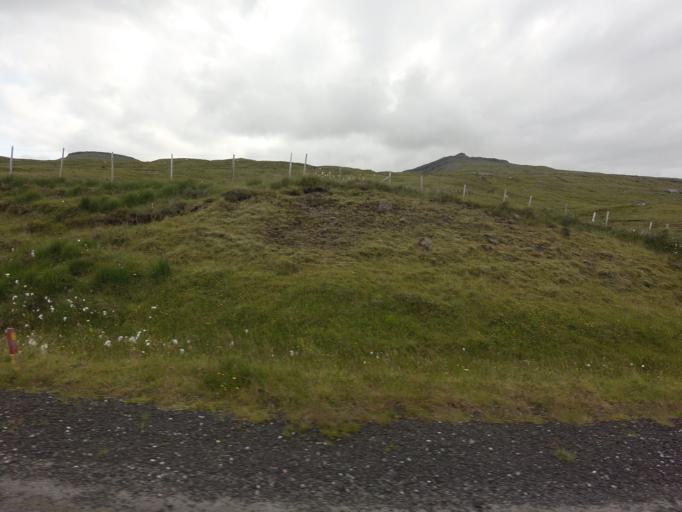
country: FO
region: Eysturoy
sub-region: Eidi
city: Eidi
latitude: 62.2151
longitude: -6.9964
